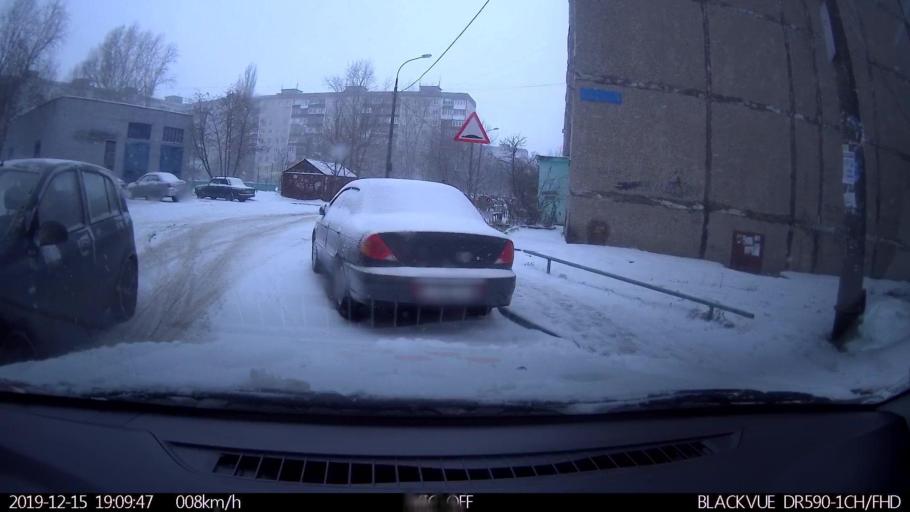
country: RU
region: Nizjnij Novgorod
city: Gorbatovka
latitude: 56.3415
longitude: 43.8412
